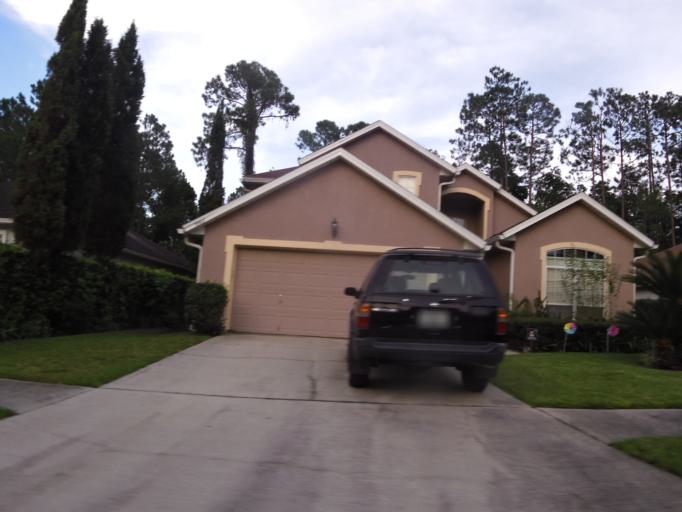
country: US
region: Florida
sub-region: Saint Johns County
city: Palm Valley
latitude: 30.2059
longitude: -81.5159
